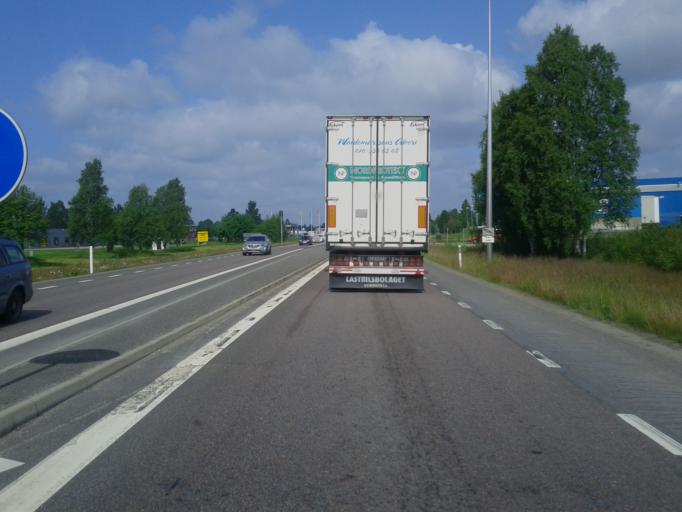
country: SE
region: Vaesterbotten
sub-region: Skelleftea Kommun
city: Skelleftea
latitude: 64.7348
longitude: 20.9686
